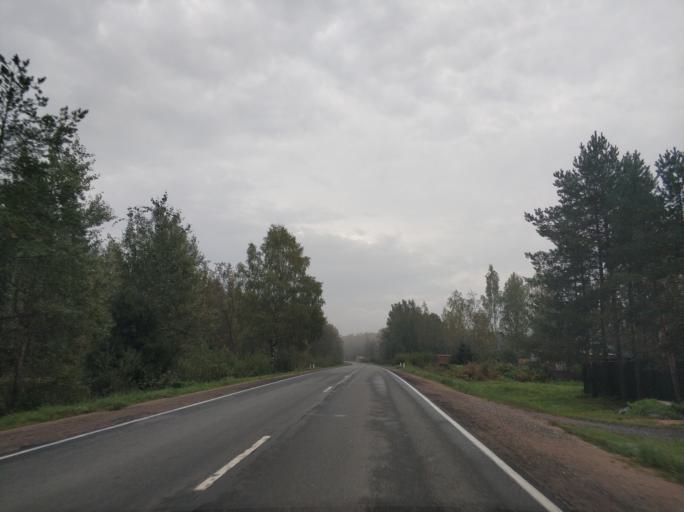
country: RU
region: Leningrad
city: Shcheglovo
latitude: 60.0948
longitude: 30.8486
